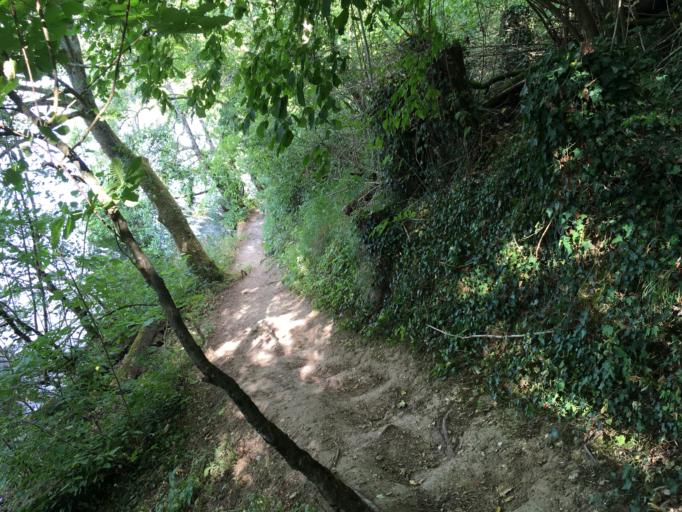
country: FR
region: Centre
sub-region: Departement d'Indre-et-Loire
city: Saint-Avertin
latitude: 47.3689
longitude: 0.7408
